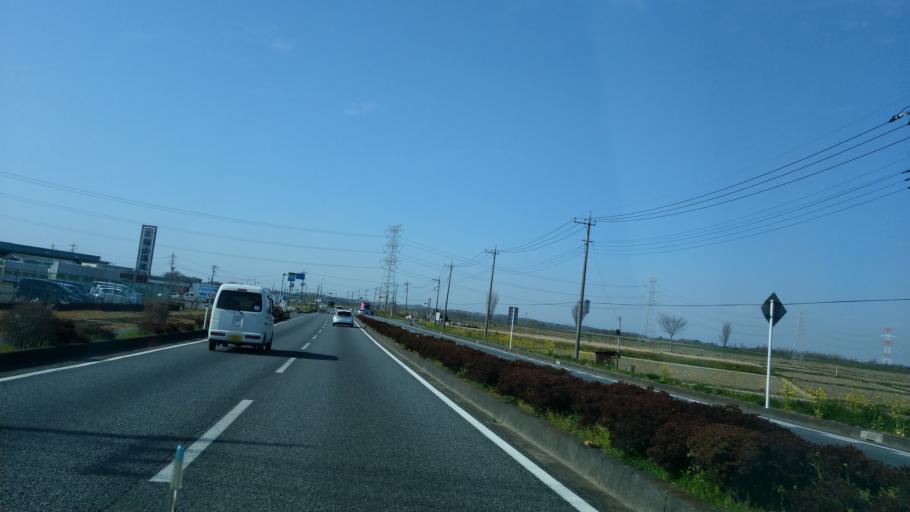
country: JP
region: Saitama
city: Sakado
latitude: 36.0000
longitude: 139.4511
